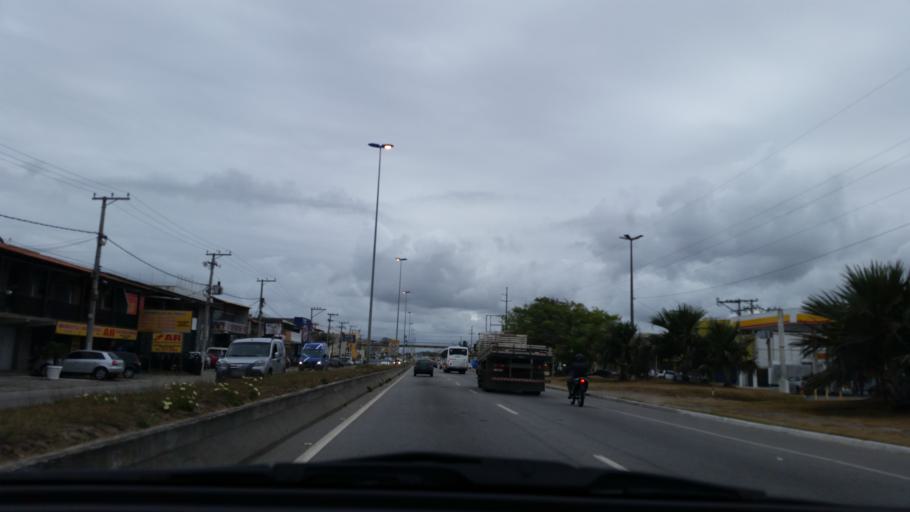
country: BR
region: Rio de Janeiro
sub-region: Sao Pedro Da Aldeia
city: Sao Pedro da Aldeia
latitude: -22.8421
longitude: -42.0712
